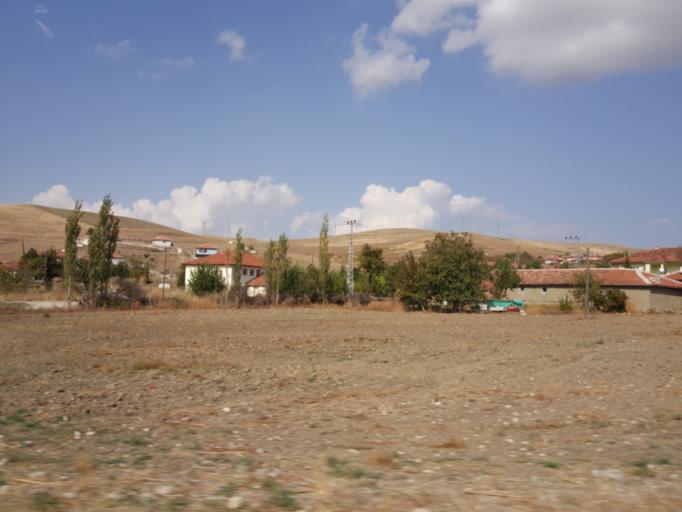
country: TR
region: Corum
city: Bogazkale
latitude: 40.1517
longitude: 34.5932
